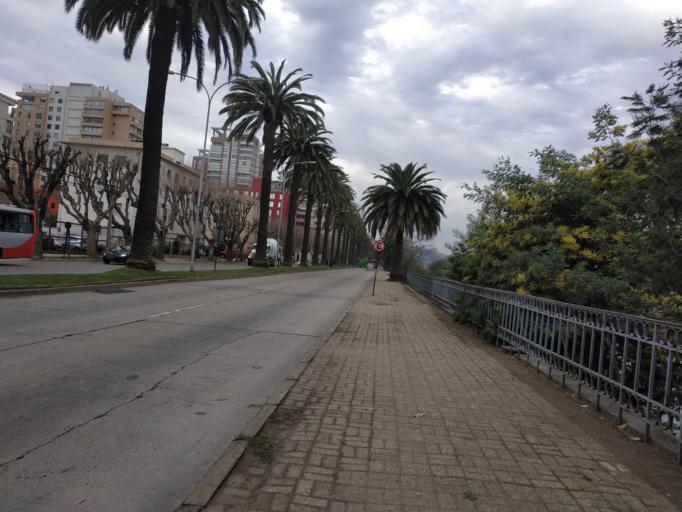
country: CL
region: Valparaiso
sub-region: Provincia de Valparaiso
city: Vina del Mar
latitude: -33.0219
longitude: -71.5561
